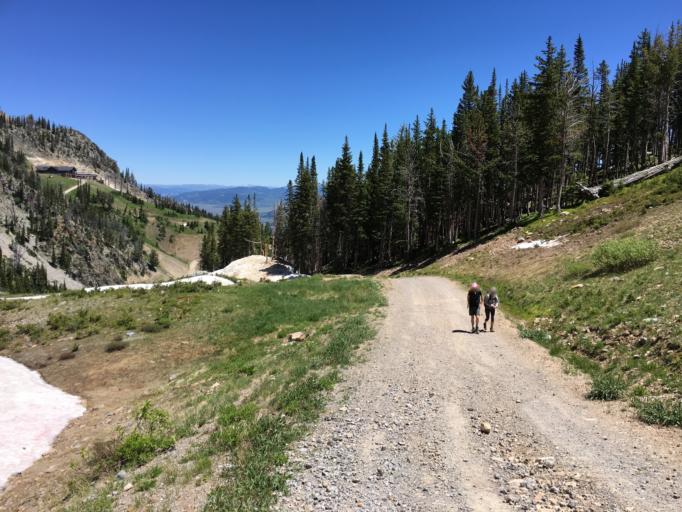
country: US
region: Wyoming
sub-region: Teton County
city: Moose Wilson Road
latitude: 43.5967
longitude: -110.8607
